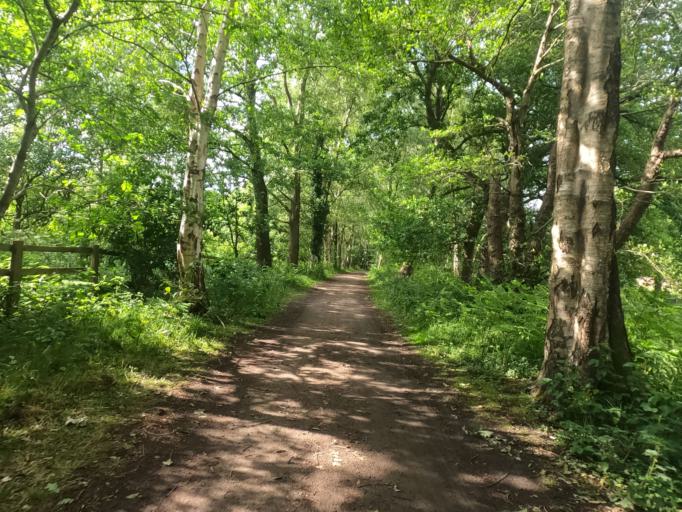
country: GB
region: England
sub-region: Cheshire West and Chester
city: Cuddington
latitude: 53.2249
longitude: -2.6189
